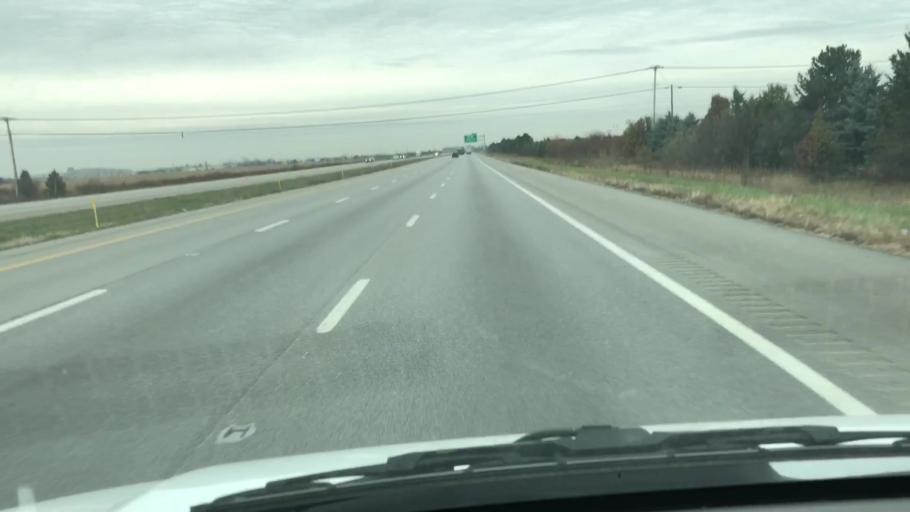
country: US
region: Ohio
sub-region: Wood County
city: Bowling Green
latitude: 41.4008
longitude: -83.6161
